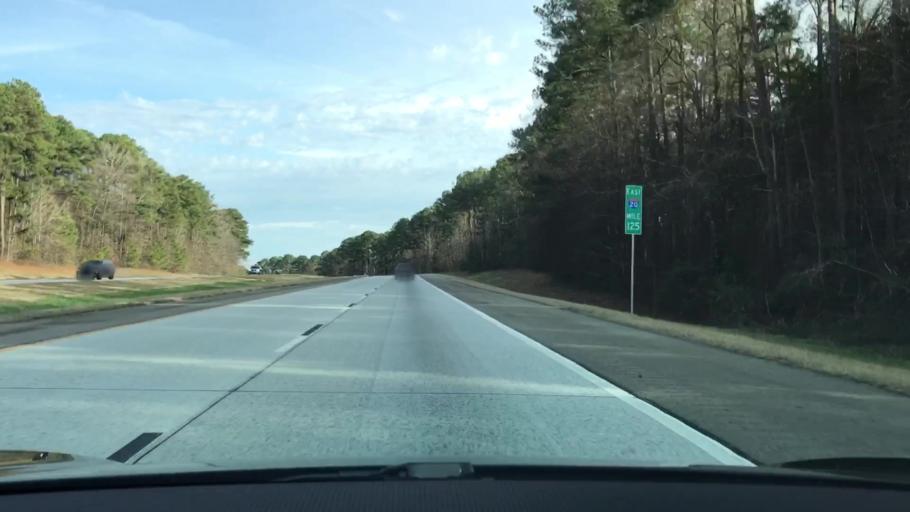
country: US
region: Georgia
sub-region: Putnam County
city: Jefferson
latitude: 33.5338
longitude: -83.2957
